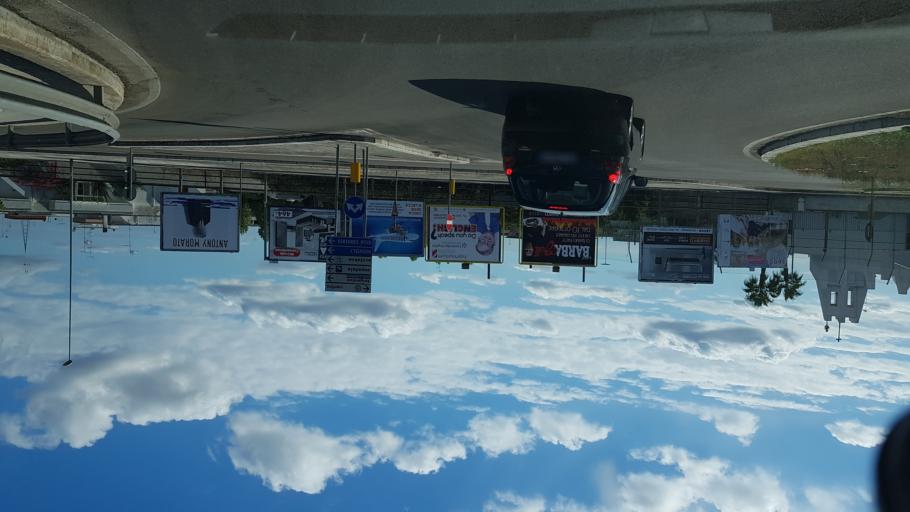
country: IT
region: Apulia
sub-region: Provincia di Lecce
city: Lecce
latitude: 40.3524
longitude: 18.1506
